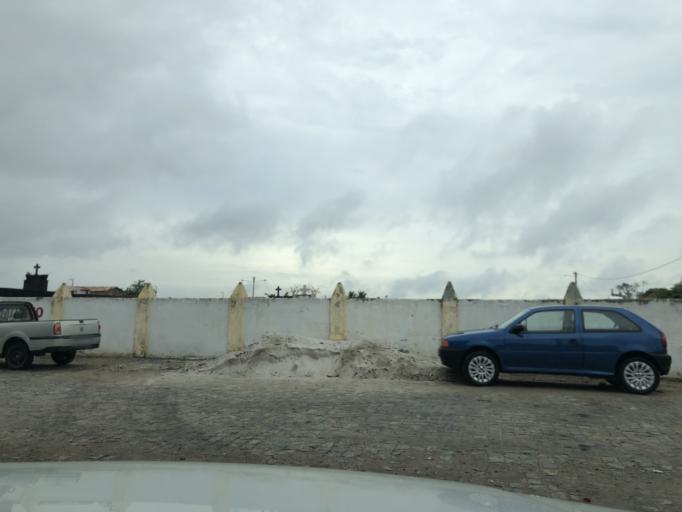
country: BR
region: Bahia
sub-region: Esplanada
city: Esplanada
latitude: -11.7936
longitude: -37.9525
